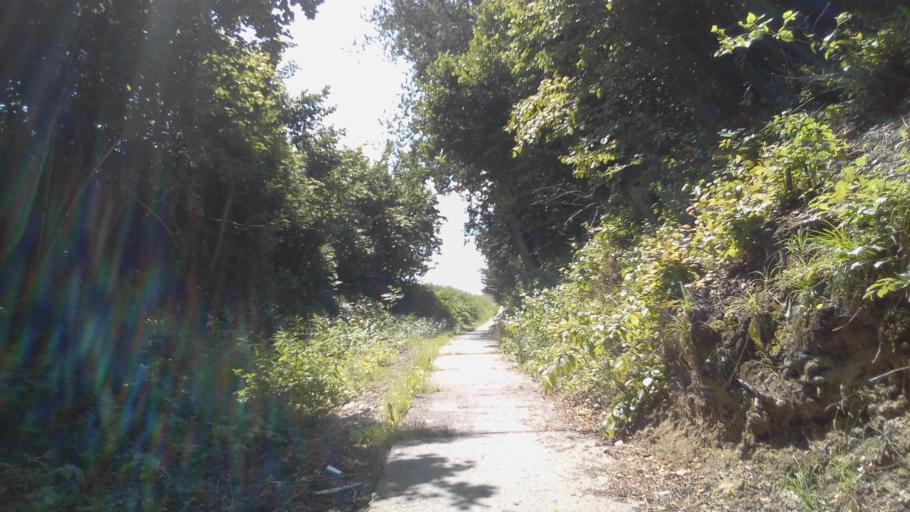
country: PL
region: Subcarpathian Voivodeship
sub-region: Powiat strzyzowski
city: Strzyzow
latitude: 49.8579
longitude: 21.7822
